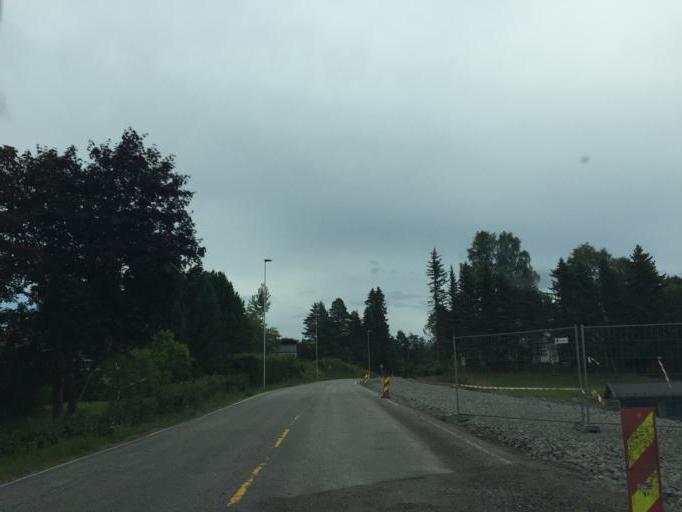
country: NO
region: Hedmark
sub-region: Kongsvinger
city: Kongsvinger
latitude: 60.2003
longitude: 11.9886
